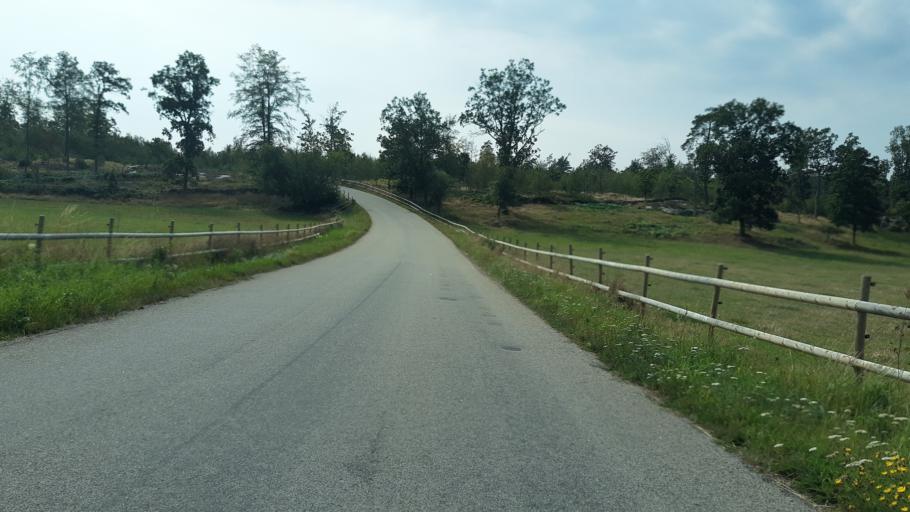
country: SE
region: Blekinge
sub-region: Karlskrona Kommun
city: Nattraby
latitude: 56.1804
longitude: 15.4950
